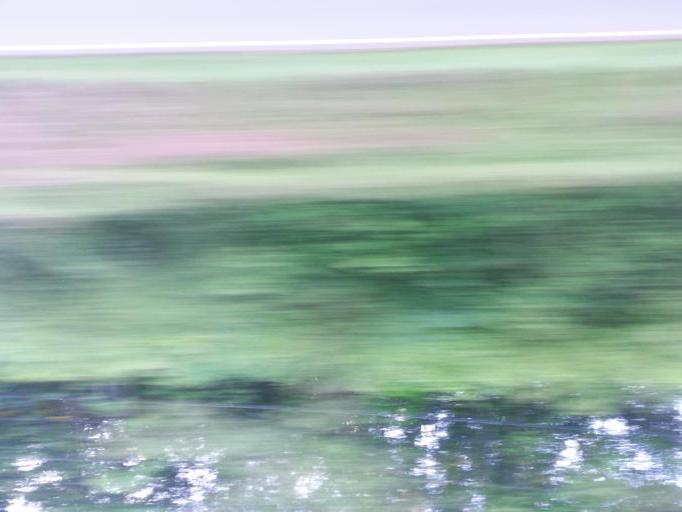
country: US
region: North Carolina
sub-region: Cherokee County
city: Murphy
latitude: 35.0958
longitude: -84.2132
